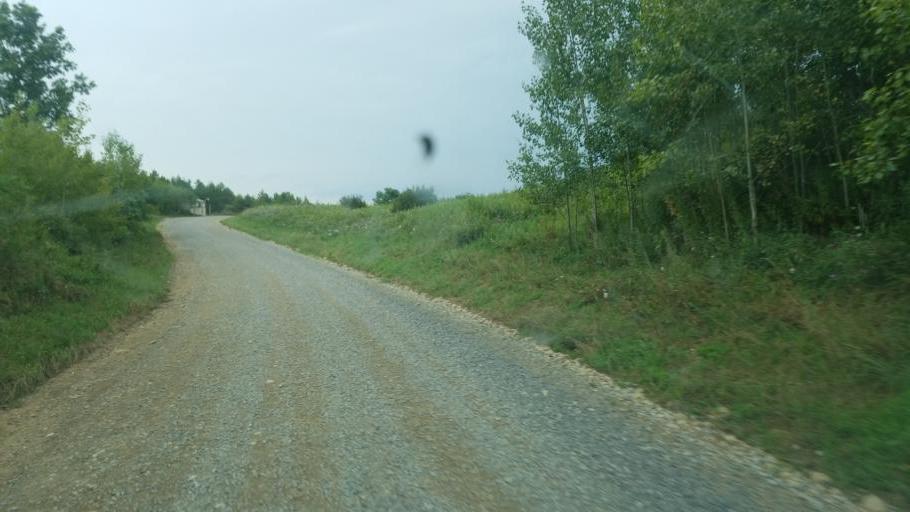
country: US
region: Pennsylvania
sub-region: Clarion County
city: Knox
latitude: 41.1509
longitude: -79.4827
